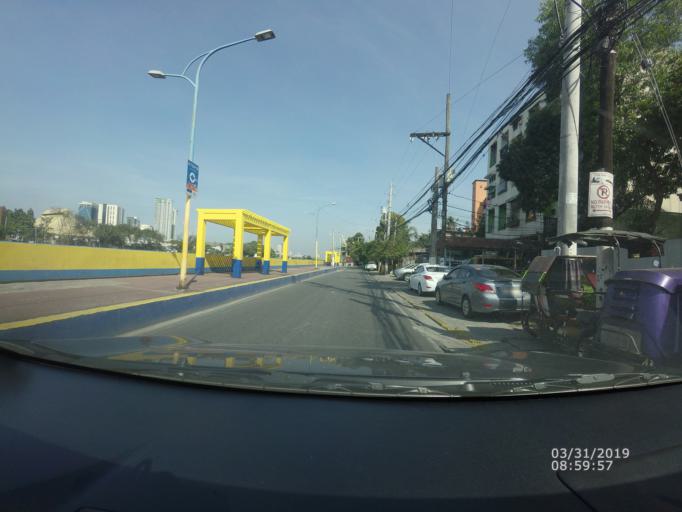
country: PH
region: Metro Manila
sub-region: Mandaluyong
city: Mandaluyong City
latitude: 14.5745
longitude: 121.0265
